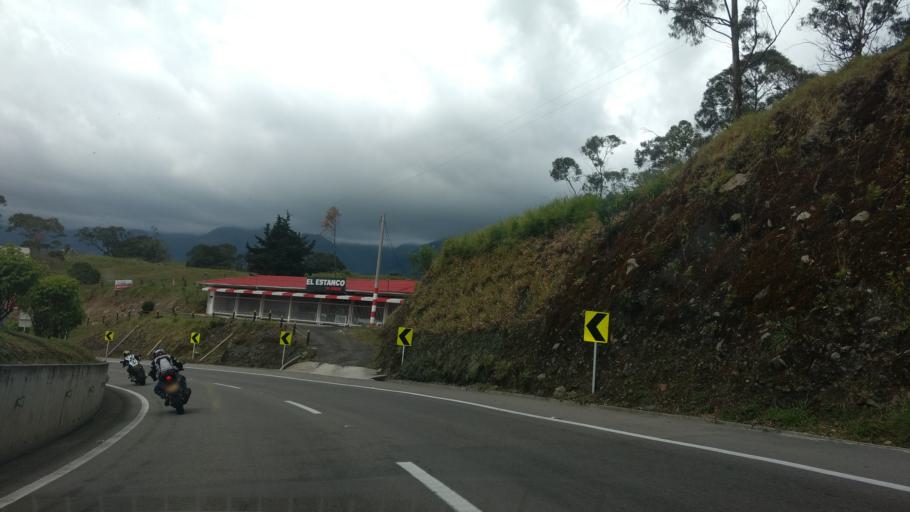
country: CO
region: Cundinamarca
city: San Francisco
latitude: 4.9442
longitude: -74.2922
